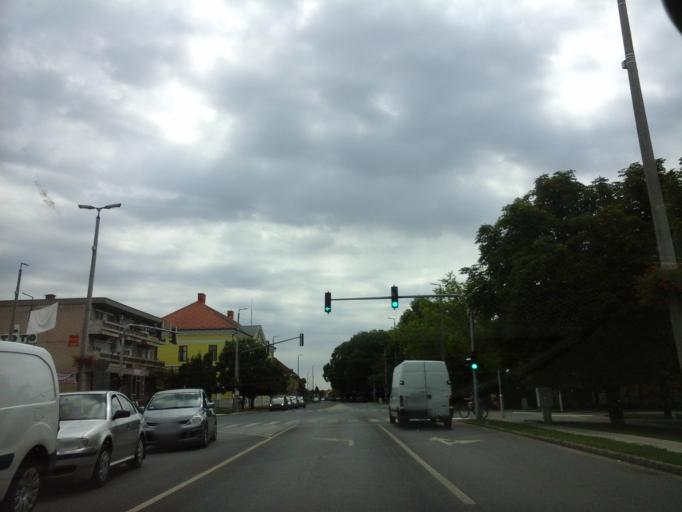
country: HU
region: Hajdu-Bihar
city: Balmazujvaros
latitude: 47.6127
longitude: 21.3430
